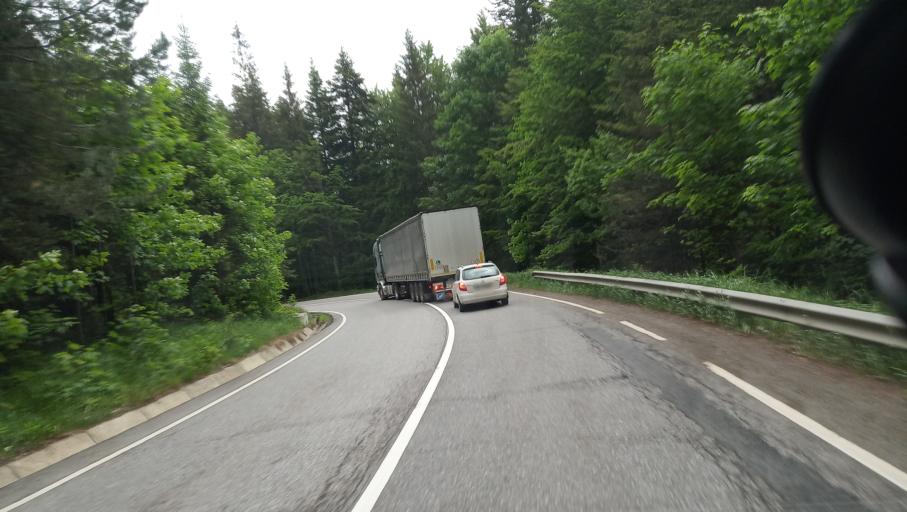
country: RO
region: Neamt
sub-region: Comuna Pipirig
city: Dolhesti
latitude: 47.1784
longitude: 26.0191
